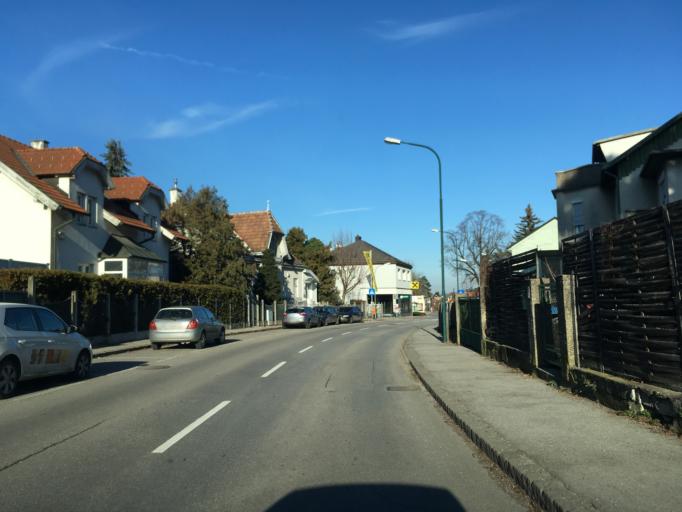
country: AT
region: Lower Austria
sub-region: Politischer Bezirk Tulln
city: Wordern
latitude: 48.3254
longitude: 16.2104
